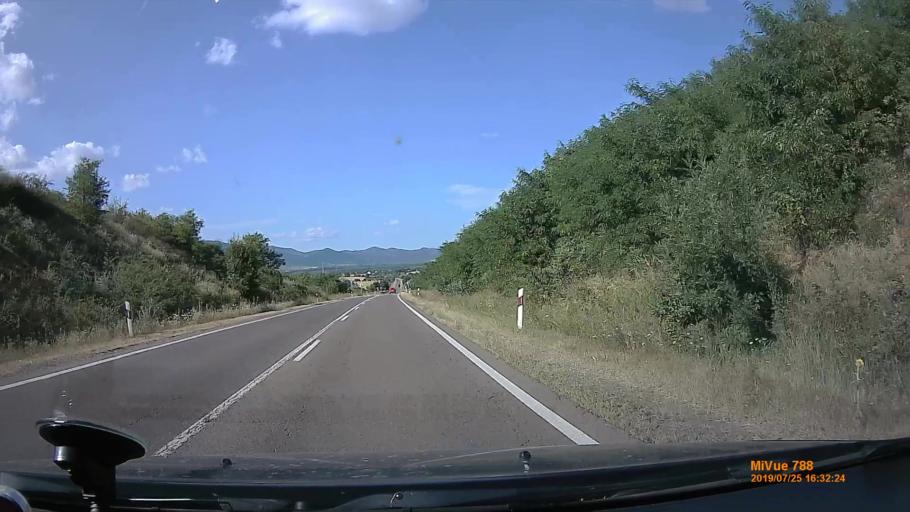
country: HU
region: Heves
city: Karacsond
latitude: 47.7473
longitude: 20.0354
